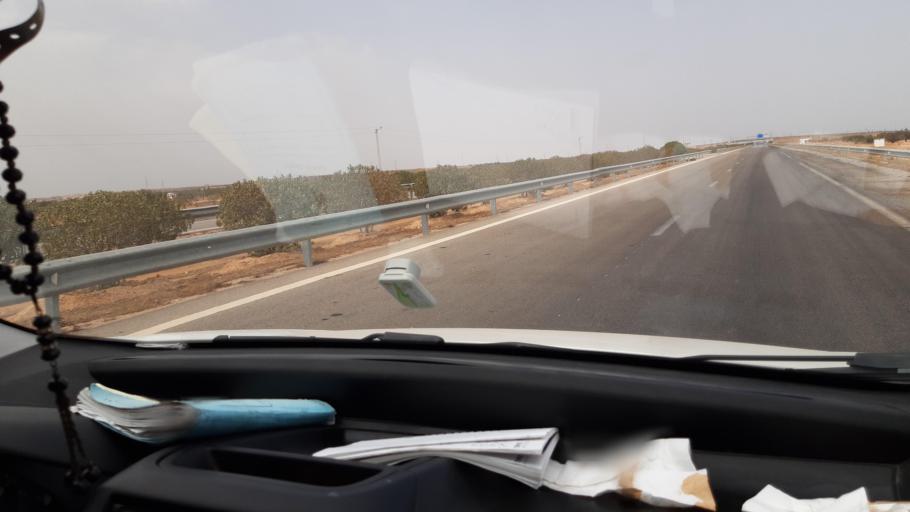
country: TN
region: Safaqis
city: Sfax
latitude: 34.8850
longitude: 10.7088
